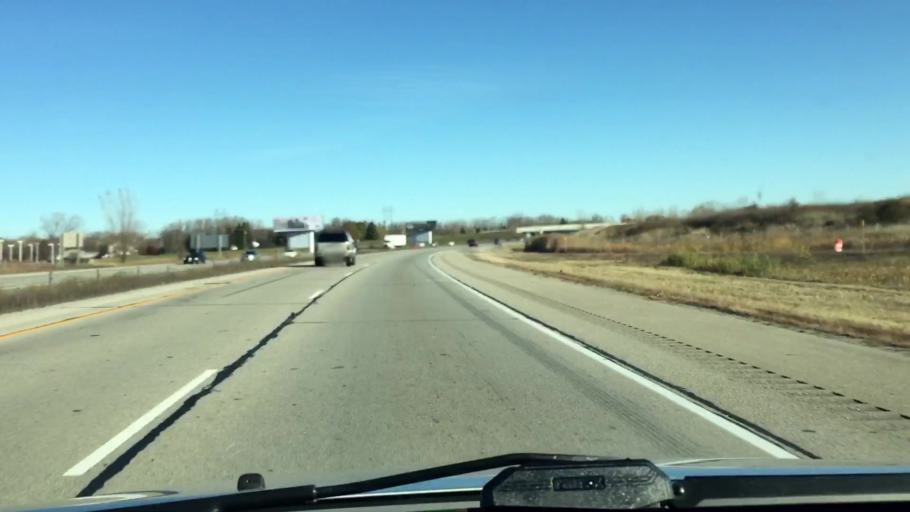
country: US
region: Wisconsin
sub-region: Outagamie County
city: Appleton
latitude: 44.2904
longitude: -88.4659
